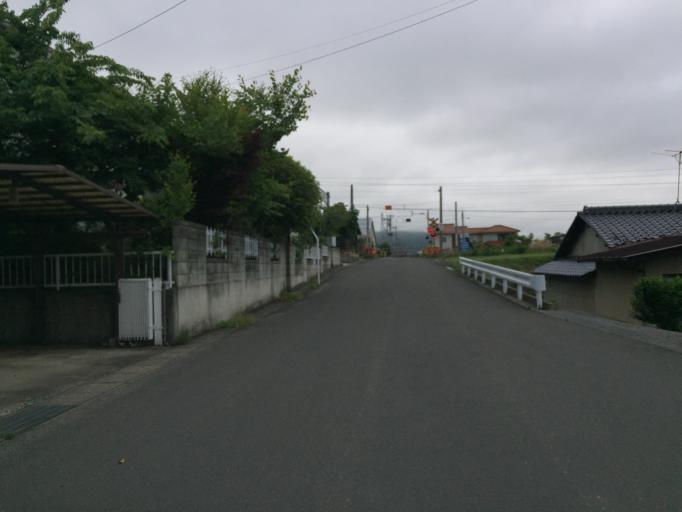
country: JP
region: Fukushima
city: Fukushima-shi
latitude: 37.7706
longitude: 140.3928
